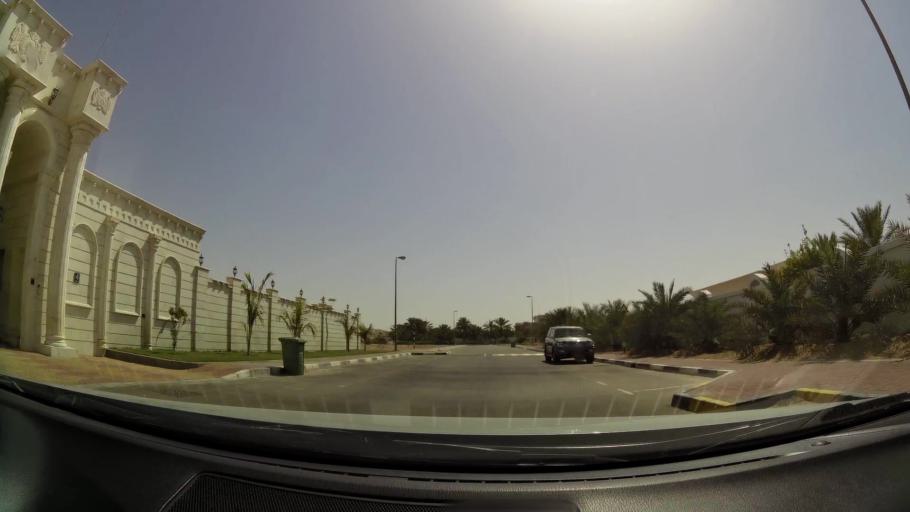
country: OM
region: Al Buraimi
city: Al Buraymi
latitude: 24.3006
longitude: 55.7547
